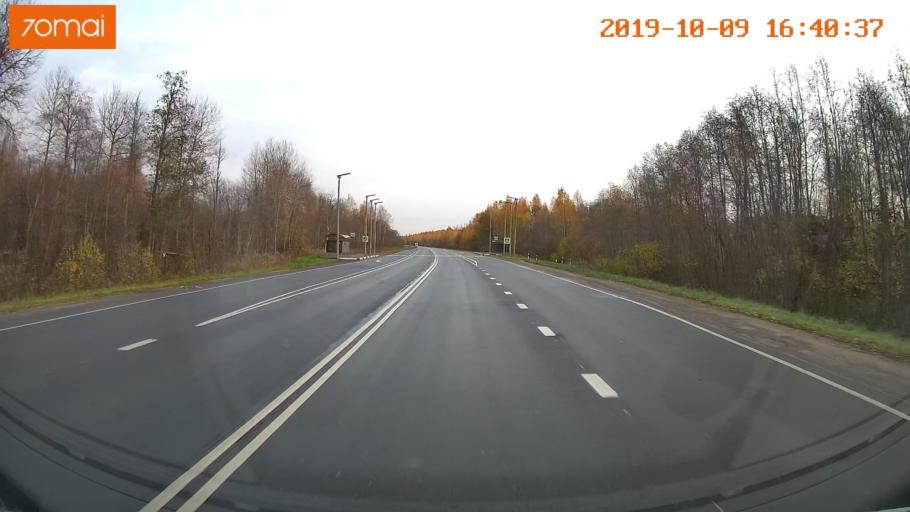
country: RU
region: Kostroma
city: Volgorechensk
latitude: 57.4814
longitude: 41.0637
